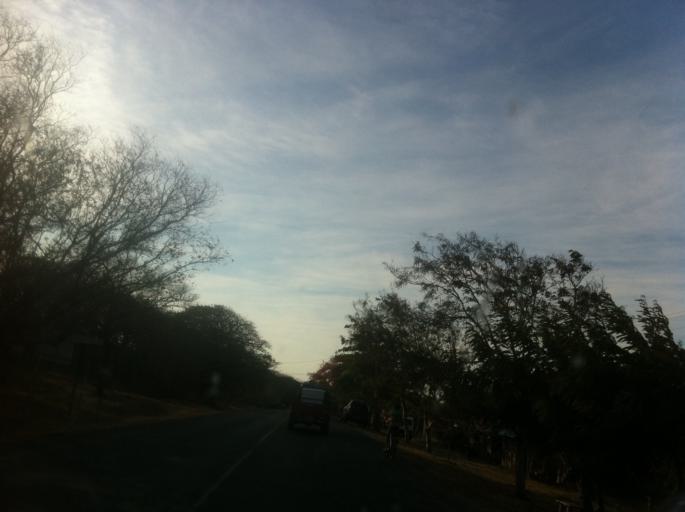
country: NI
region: Rivas
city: Rivas
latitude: 11.3557
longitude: -85.7428
